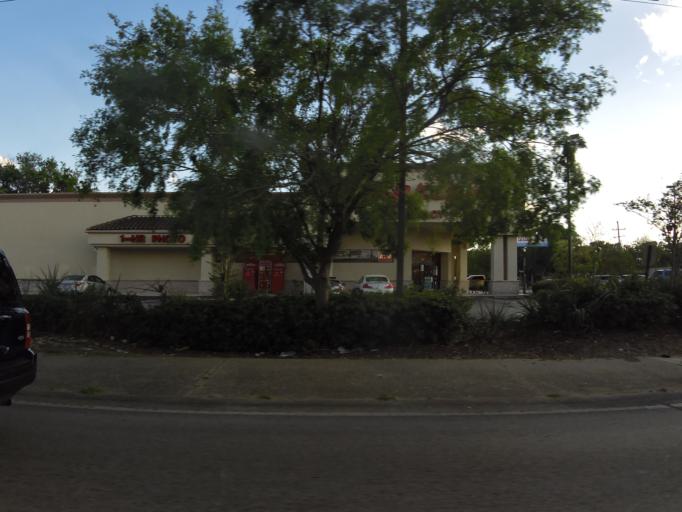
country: US
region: Florida
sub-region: Duval County
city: Jacksonville
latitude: 30.3520
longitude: -81.5772
